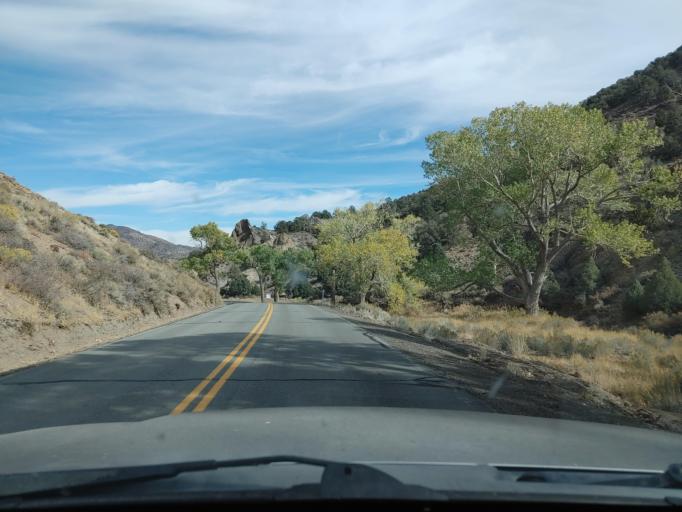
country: US
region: Nevada
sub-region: Storey County
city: Virginia City
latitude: 39.3051
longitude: -119.6069
